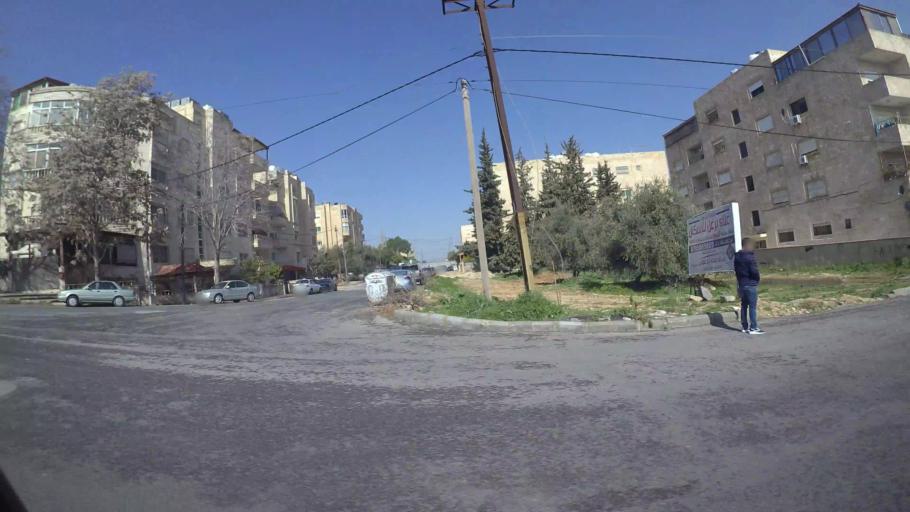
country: JO
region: Amman
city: Al Bunayyat ash Shamaliyah
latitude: 31.9215
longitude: 35.8958
